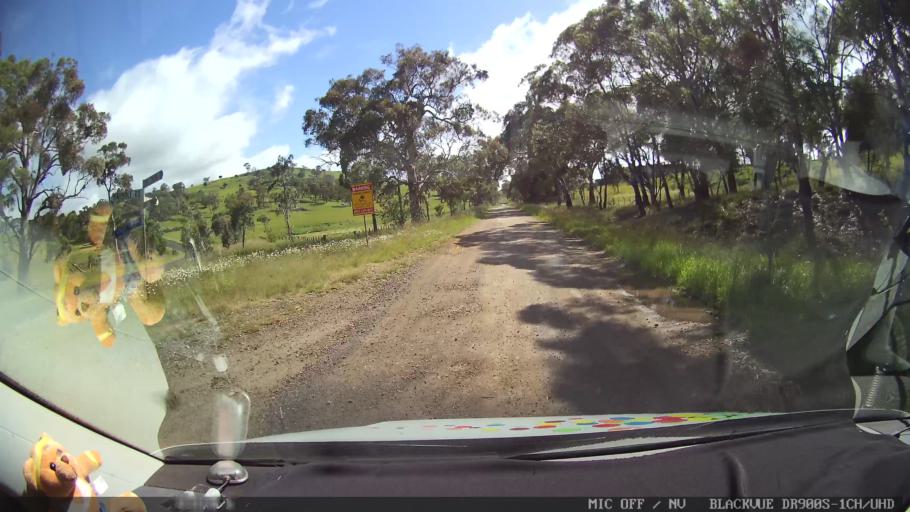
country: AU
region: New South Wales
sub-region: Guyra
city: Guyra
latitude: -30.0116
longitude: 151.6586
